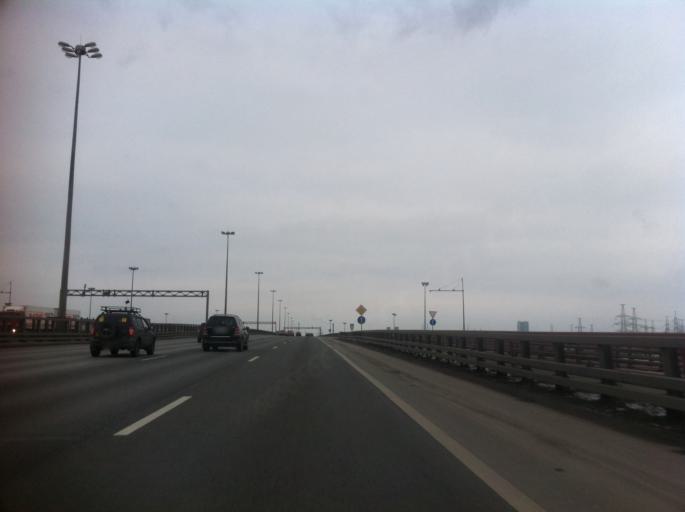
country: RU
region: St.-Petersburg
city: Obukhovo
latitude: 59.8284
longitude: 30.4397
